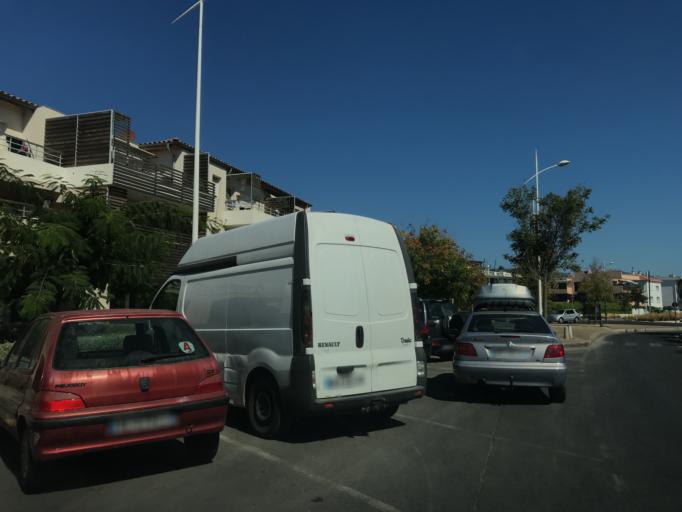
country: FR
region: Provence-Alpes-Cote d'Azur
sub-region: Departement du Var
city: La Seyne-sur-Mer
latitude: 43.0805
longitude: 5.8940
